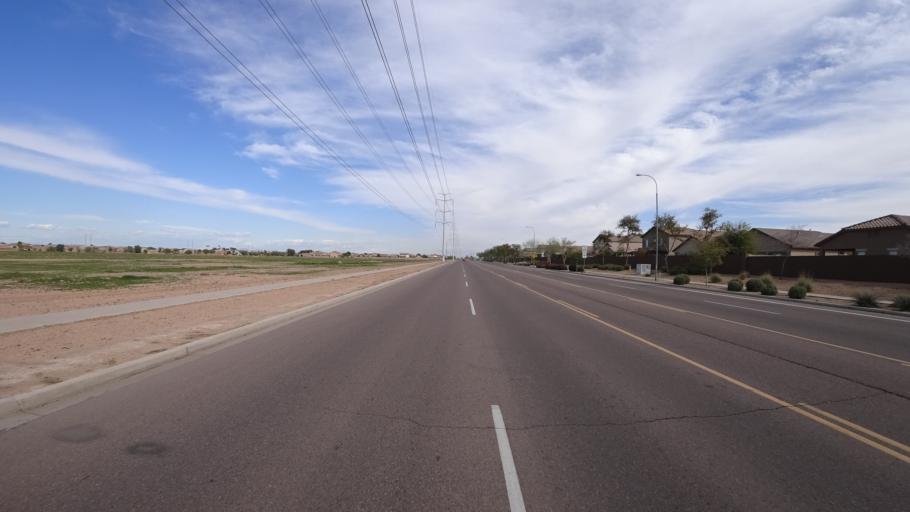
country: US
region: Arizona
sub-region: Maricopa County
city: Tolleson
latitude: 33.4065
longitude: -112.2800
